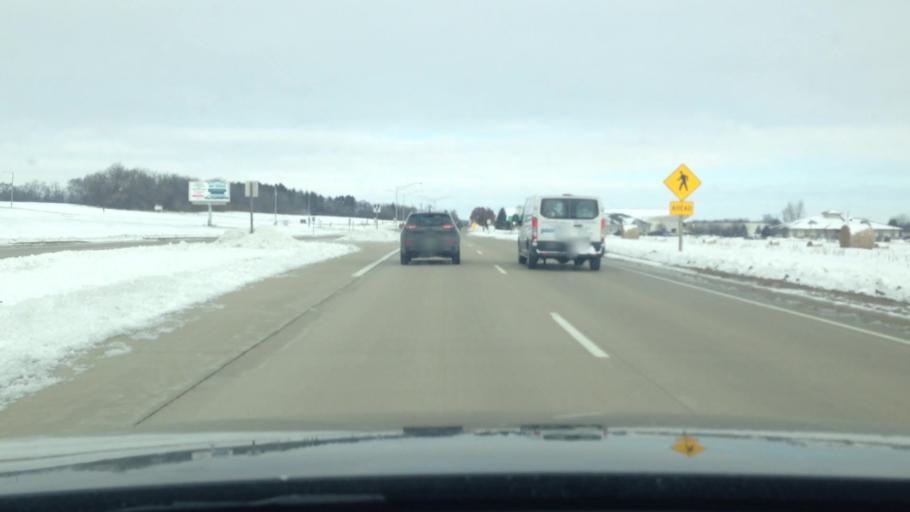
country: US
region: Wisconsin
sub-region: Walworth County
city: Lake Geneva
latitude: 42.5799
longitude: -88.4117
